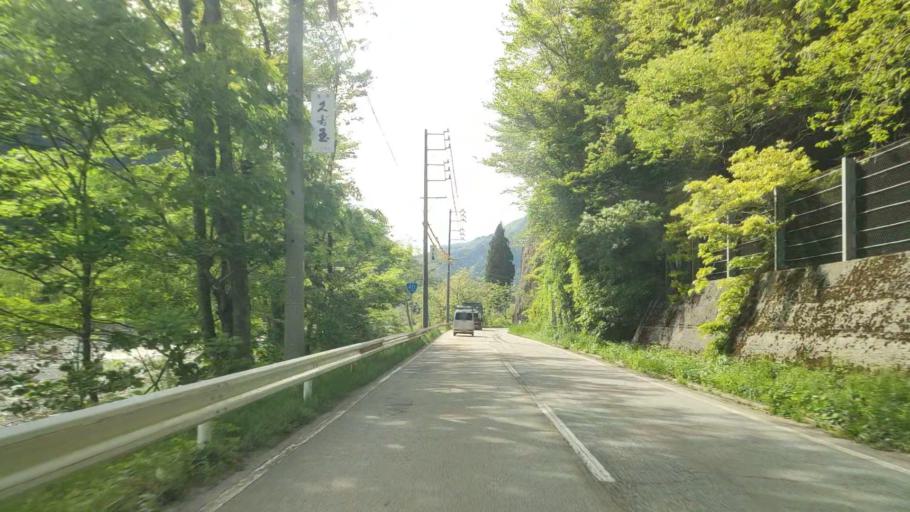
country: JP
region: Gifu
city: Takayama
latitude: 36.2515
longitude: 137.4799
